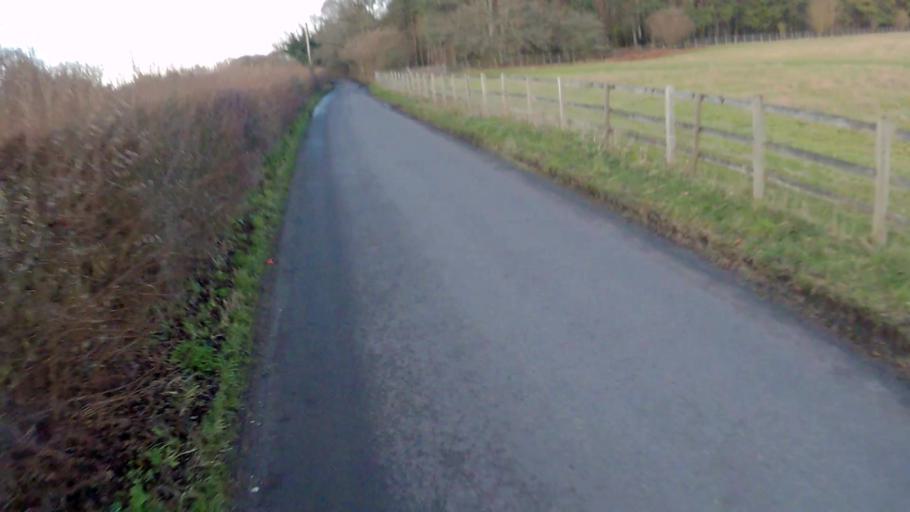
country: GB
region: England
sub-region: Hampshire
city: Overton
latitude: 51.2334
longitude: -1.2186
